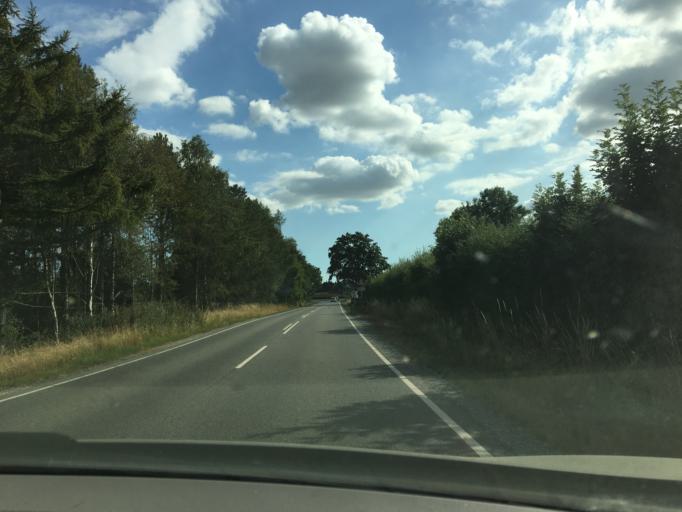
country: DK
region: South Denmark
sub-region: Nordfyns Kommune
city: Sonderso
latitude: 55.4517
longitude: 10.1873
